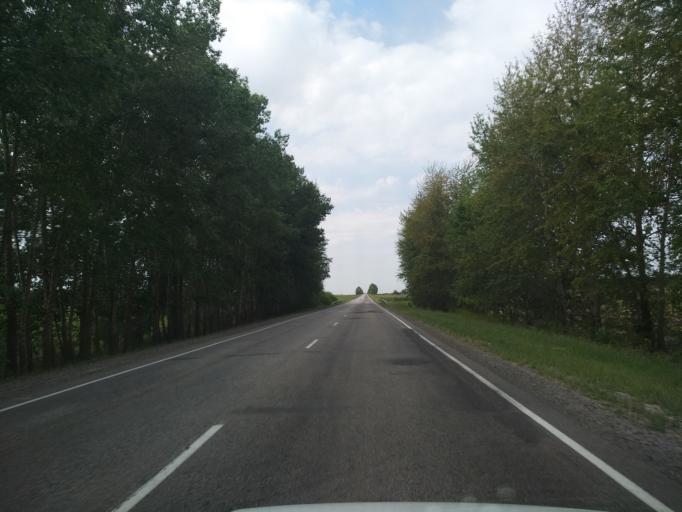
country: RU
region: Voronezj
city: Pereleshino
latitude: 51.7265
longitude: 40.0467
